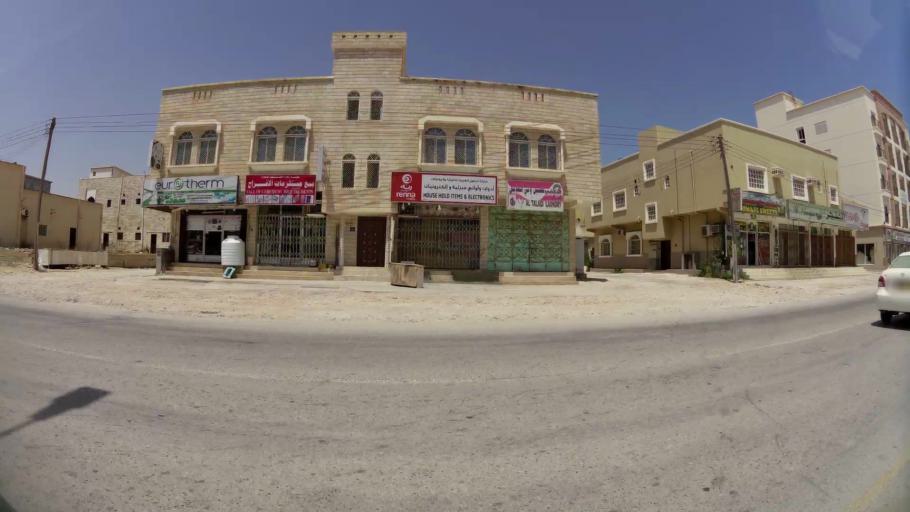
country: OM
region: Zufar
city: Salalah
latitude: 17.0125
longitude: 54.0792
